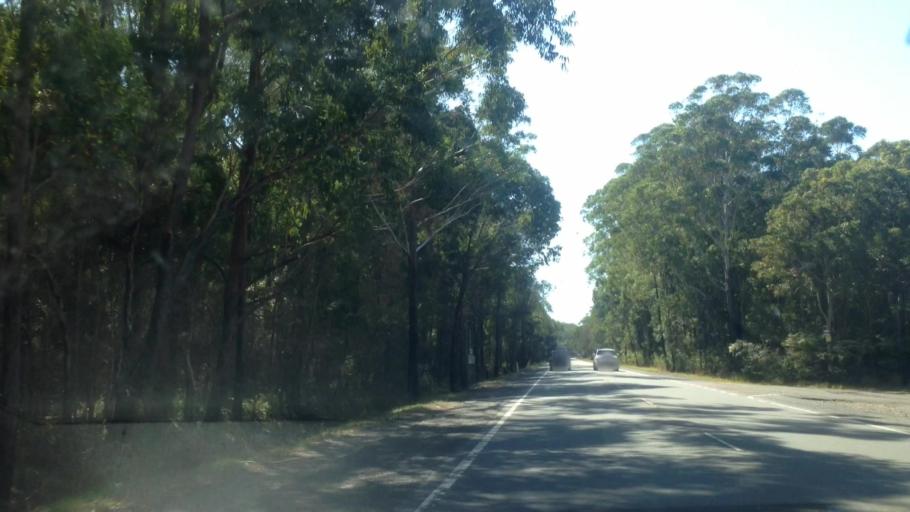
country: AU
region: New South Wales
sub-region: Lake Macquarie Shire
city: Toronto
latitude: -32.9873
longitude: 151.5084
